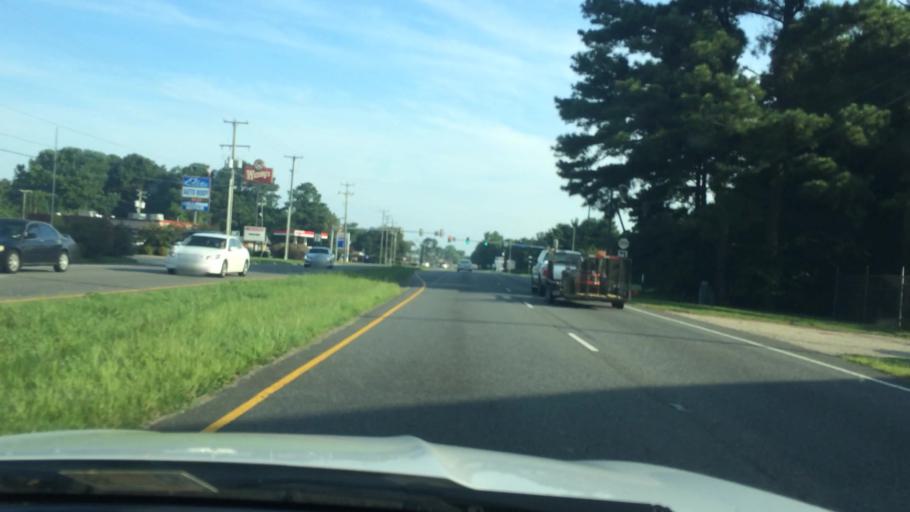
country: US
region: Virginia
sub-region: Gloucester County
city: Gloucester Point
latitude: 37.2897
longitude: -76.5089
